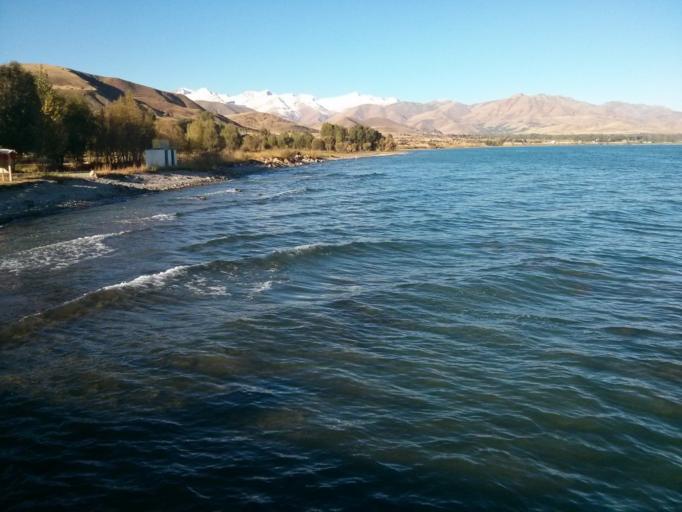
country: TR
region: Van
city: Gevas
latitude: 38.3092
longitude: 43.0267
